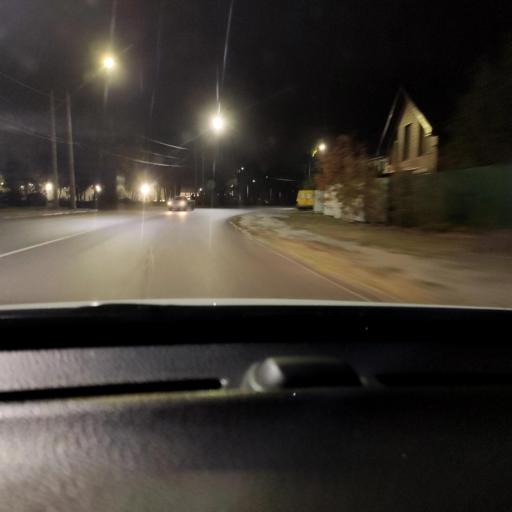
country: RU
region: Voronezj
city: Voronezh
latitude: 51.7314
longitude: 39.2600
